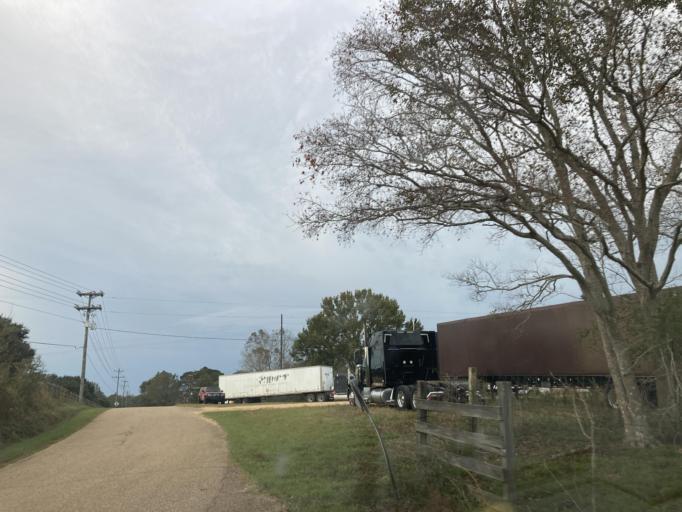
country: US
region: Mississippi
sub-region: Lamar County
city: Purvis
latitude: 31.1675
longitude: -89.3876
